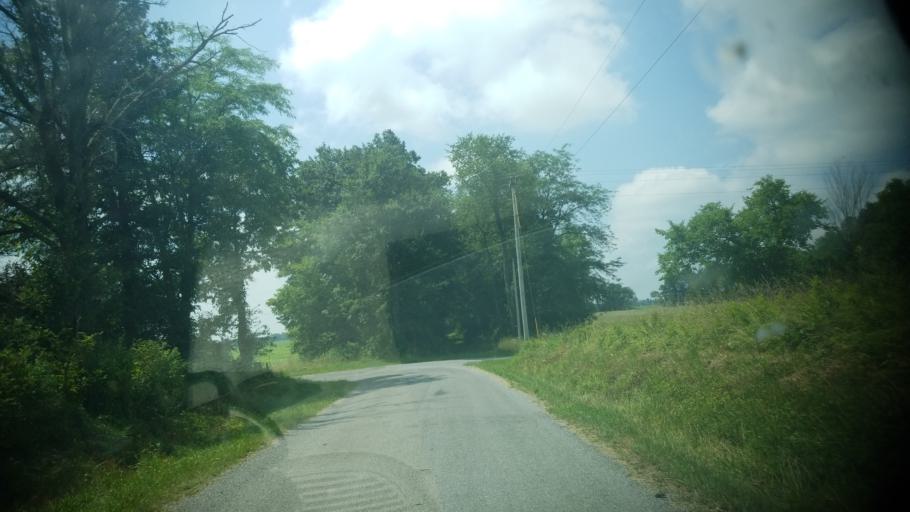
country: US
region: Illinois
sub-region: Wayne County
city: Fairfield
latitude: 38.5227
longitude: -88.3656
